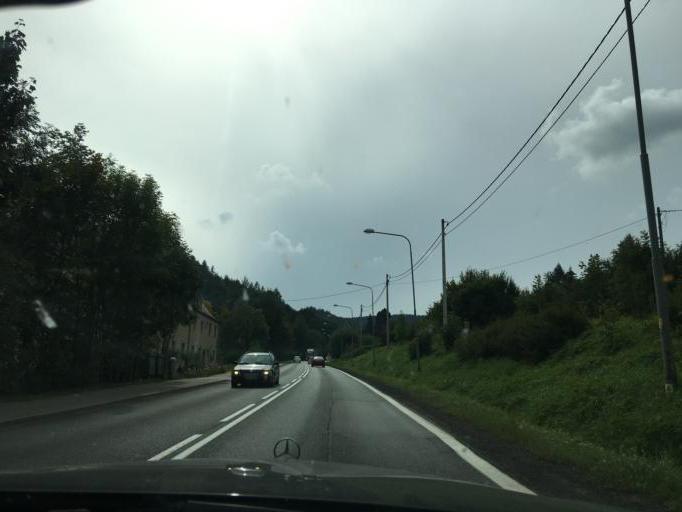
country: PL
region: Lower Silesian Voivodeship
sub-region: Powiat klodzki
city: Duszniki-Zdroj
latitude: 50.4041
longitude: 16.3837
